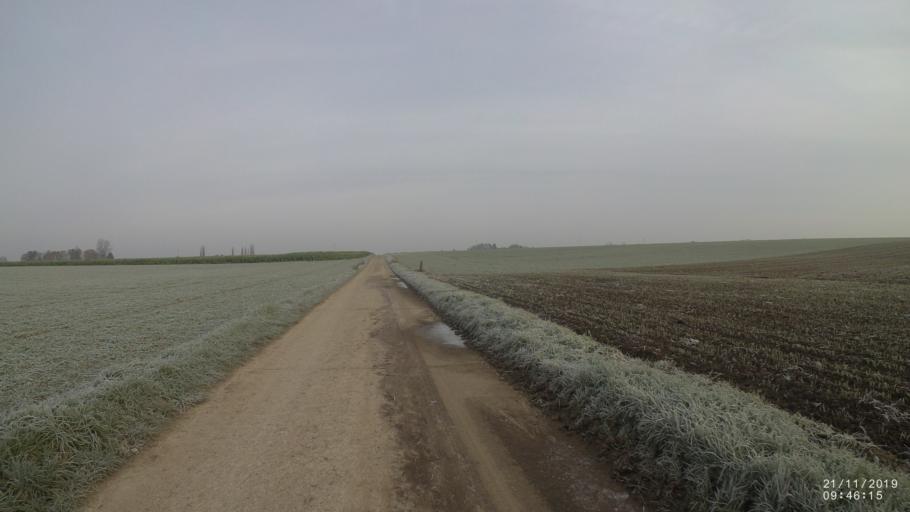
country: BE
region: Flanders
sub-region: Provincie Vlaams-Brabant
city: Tienen
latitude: 50.7918
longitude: 5.0036
